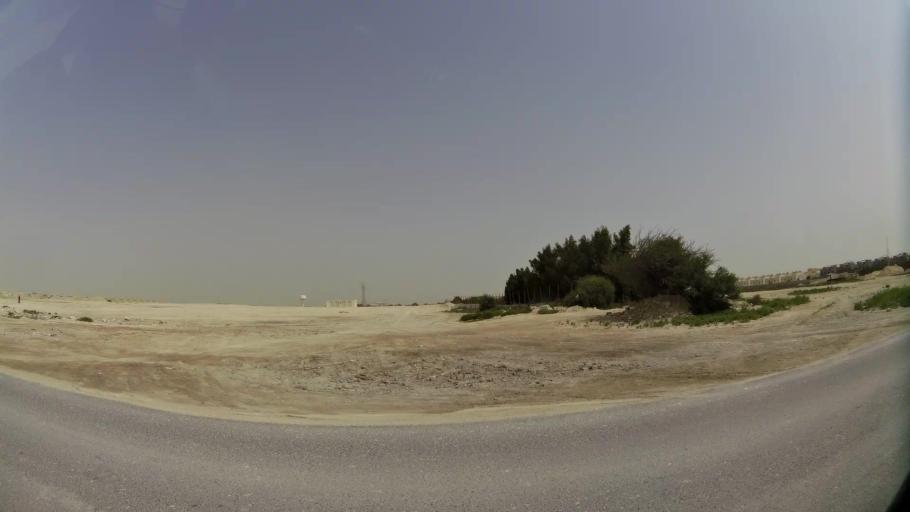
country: QA
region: Baladiyat ar Rayyan
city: Ar Rayyan
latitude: 25.2331
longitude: 51.4070
